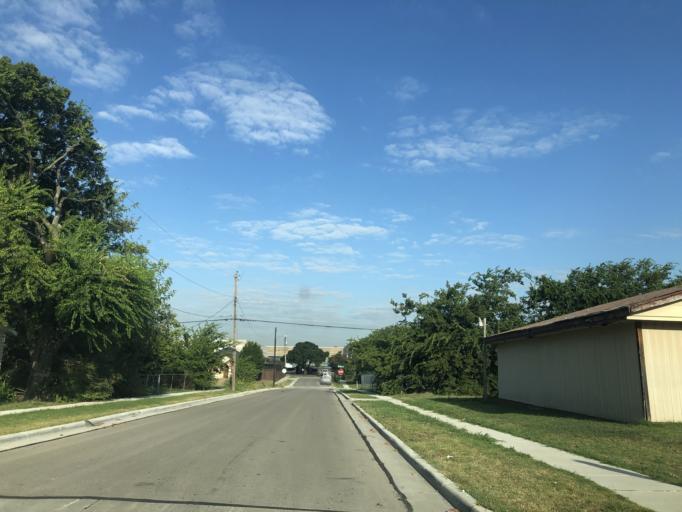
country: US
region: Texas
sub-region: Dallas County
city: Grand Prairie
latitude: 32.7331
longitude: -97.0384
